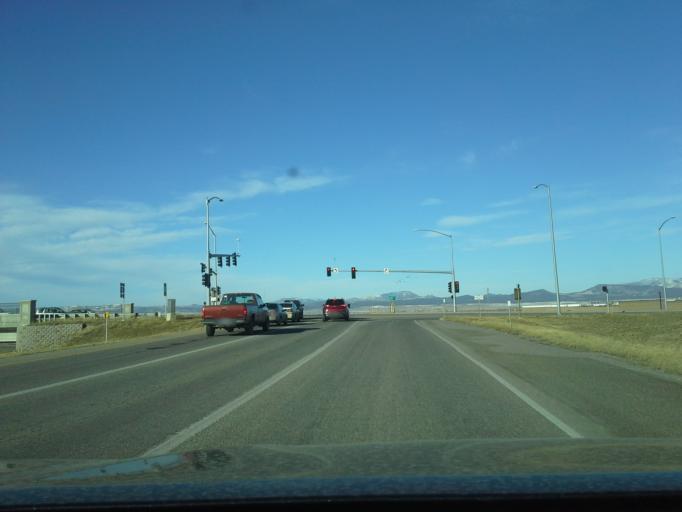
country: US
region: Montana
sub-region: Lewis and Clark County
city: Helena
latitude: 46.6159
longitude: -112.0099
